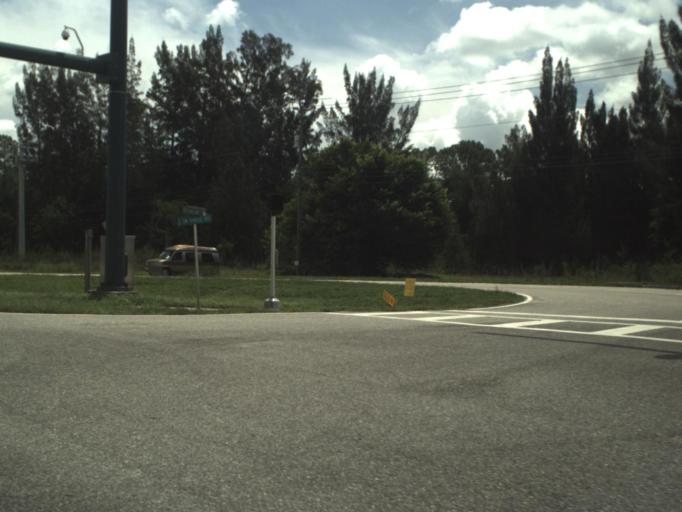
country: US
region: Florida
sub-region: Martin County
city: Palm City
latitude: 27.1021
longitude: -80.2685
